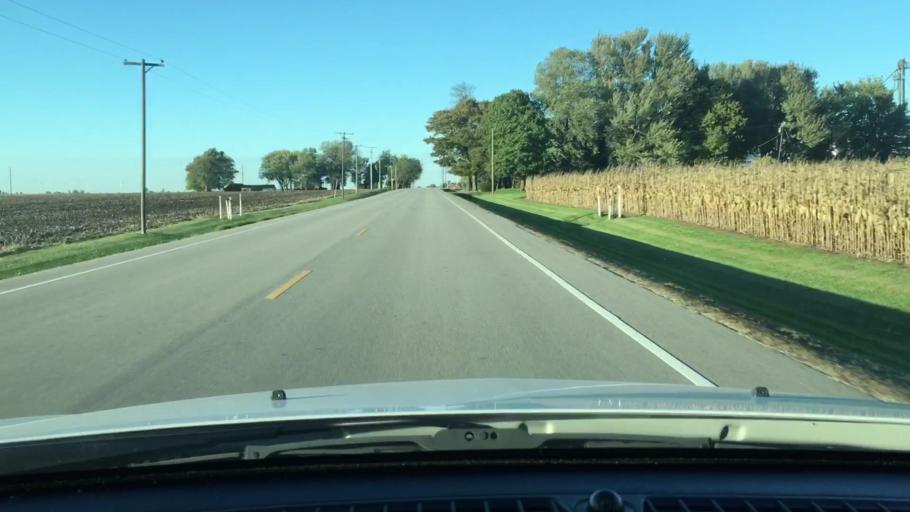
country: US
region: Illinois
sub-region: DeKalb County
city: Malta
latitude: 41.8200
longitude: -88.8864
